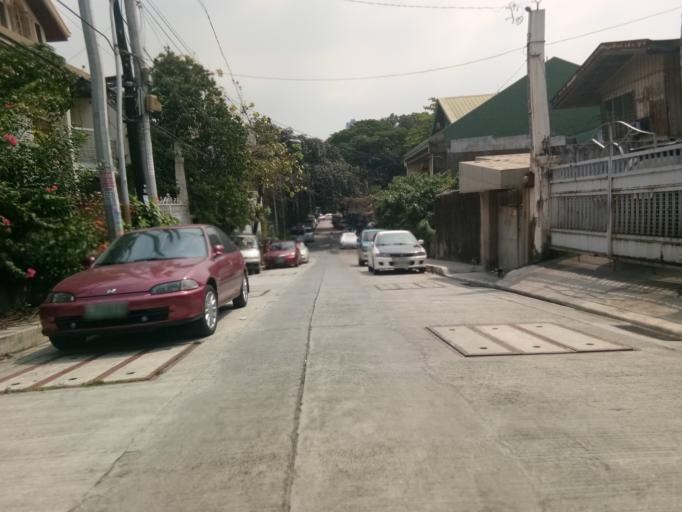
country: PH
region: Metro Manila
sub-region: San Juan
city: San Juan
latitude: 14.6138
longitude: 121.0521
